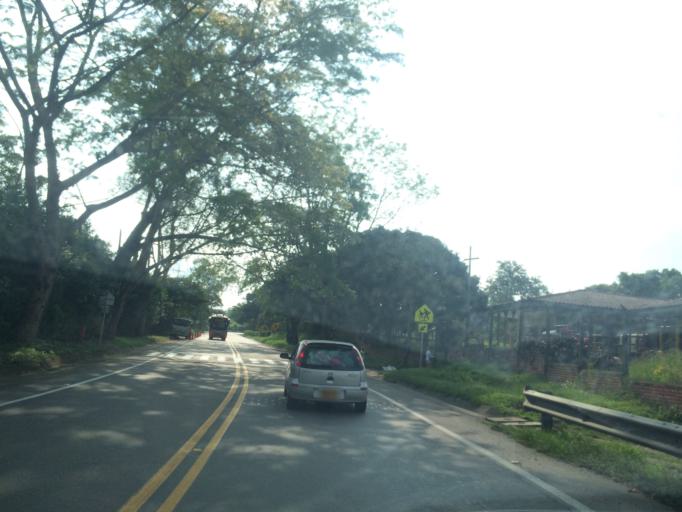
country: CO
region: Quindio
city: La Tebaida
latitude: 4.4494
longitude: -75.8169
